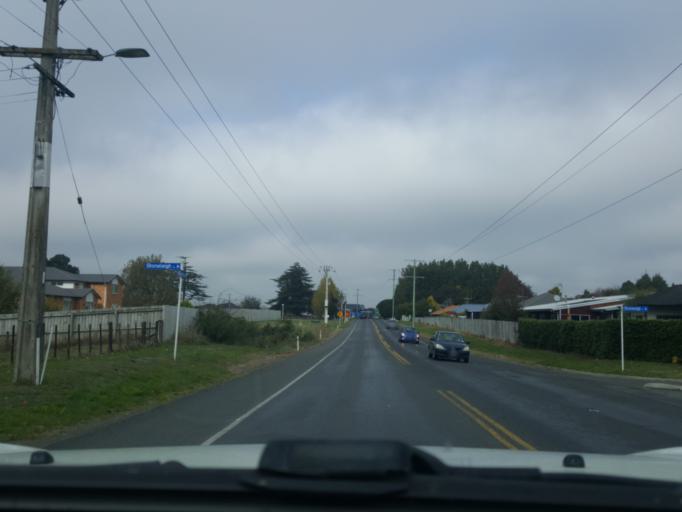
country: NZ
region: Waikato
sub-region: Hamilton City
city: Hamilton
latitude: -37.7461
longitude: 175.2922
